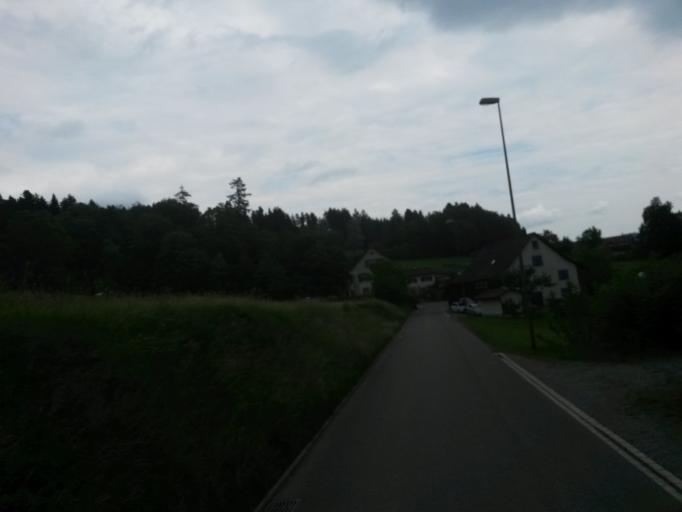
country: CH
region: Zurich
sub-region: Bezirk Pfaeffikon
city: Pfaffikon
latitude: 47.3797
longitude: 8.8040
